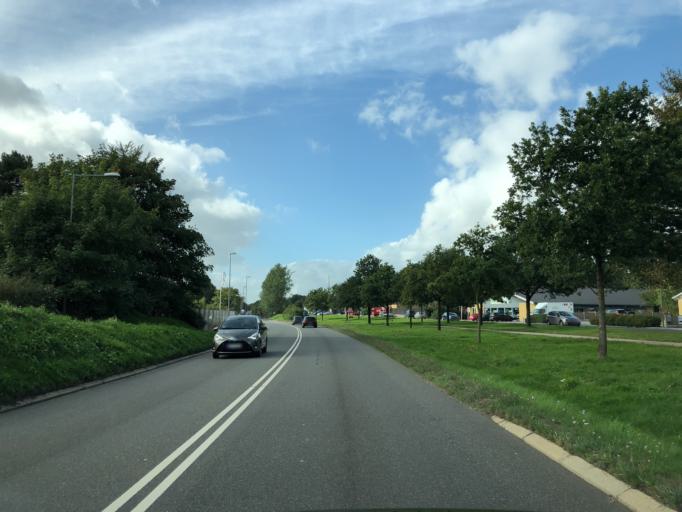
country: DK
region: Central Jutland
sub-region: Holstebro Kommune
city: Holstebro
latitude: 56.3646
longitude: 8.5906
